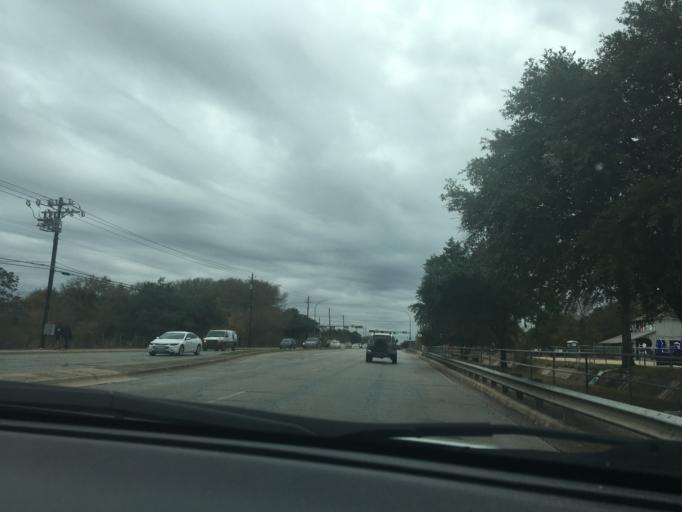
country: US
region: Texas
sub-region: Travis County
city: Rollingwood
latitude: 30.2212
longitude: -97.8259
